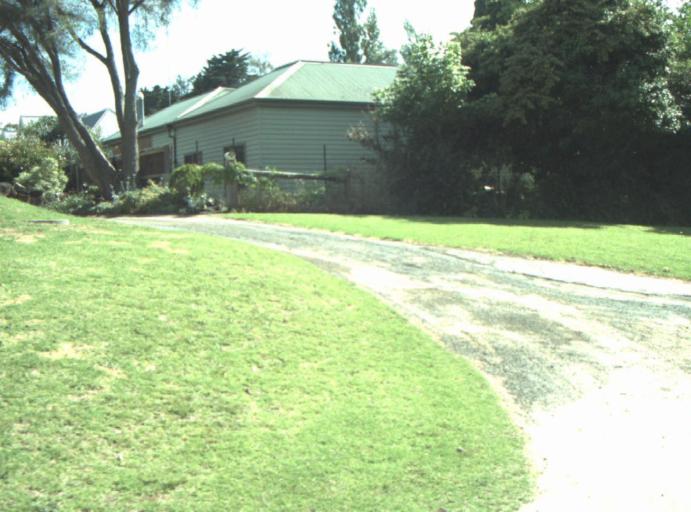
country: AU
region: Victoria
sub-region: Greater Geelong
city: Clifton Springs
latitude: -38.1721
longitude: 144.5617
